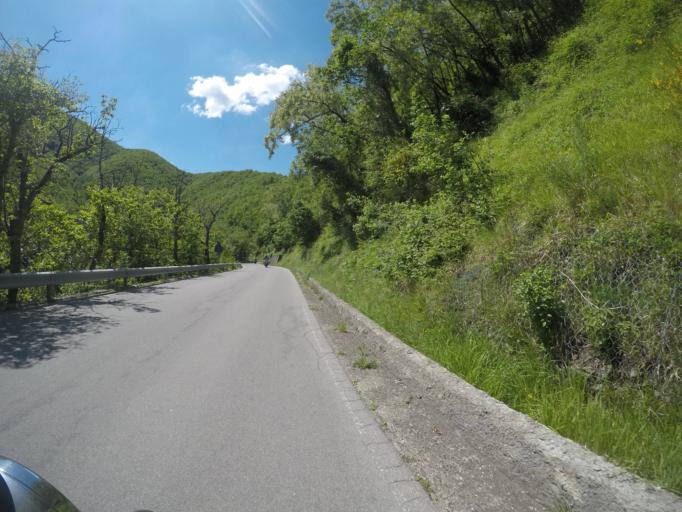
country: IT
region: Tuscany
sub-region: Provincia di Lucca
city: Careggine
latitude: 44.1251
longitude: 10.3307
